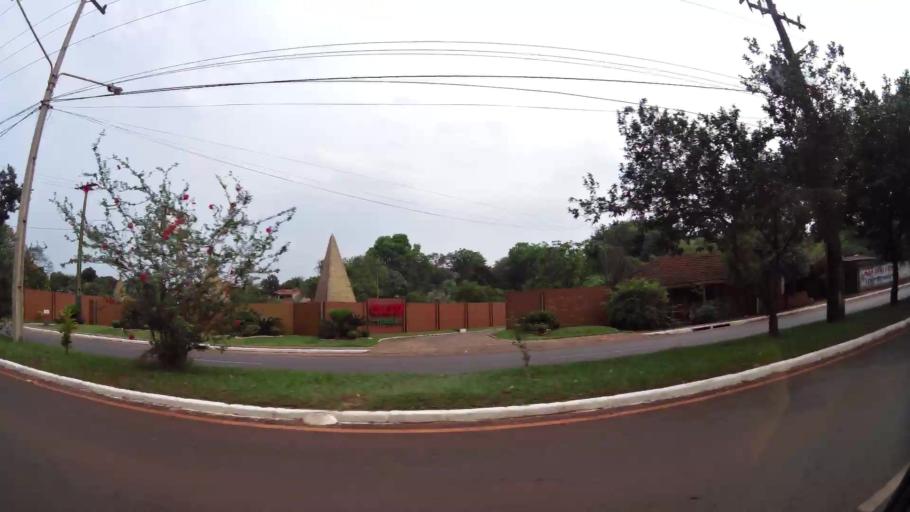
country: PY
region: Alto Parana
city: Presidente Franco
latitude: -25.5490
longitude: -54.6223
